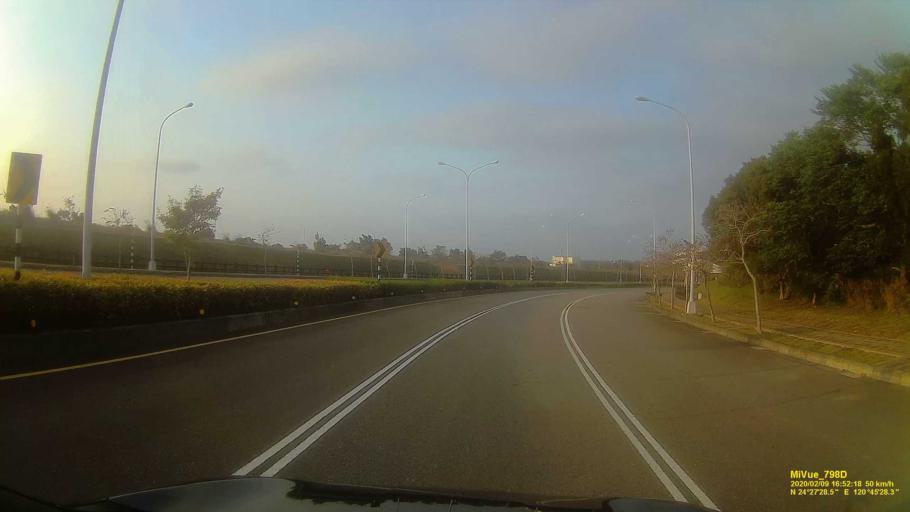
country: TW
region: Taiwan
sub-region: Miaoli
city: Miaoli
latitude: 24.4581
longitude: 120.7578
